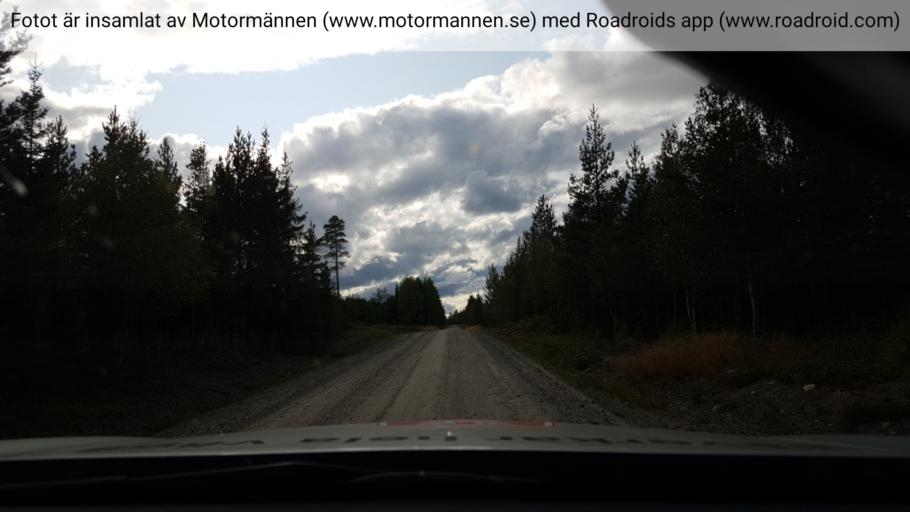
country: SE
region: Vaesterbotten
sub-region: Lycksele Kommun
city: Lycksele
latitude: 64.7088
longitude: 18.8183
